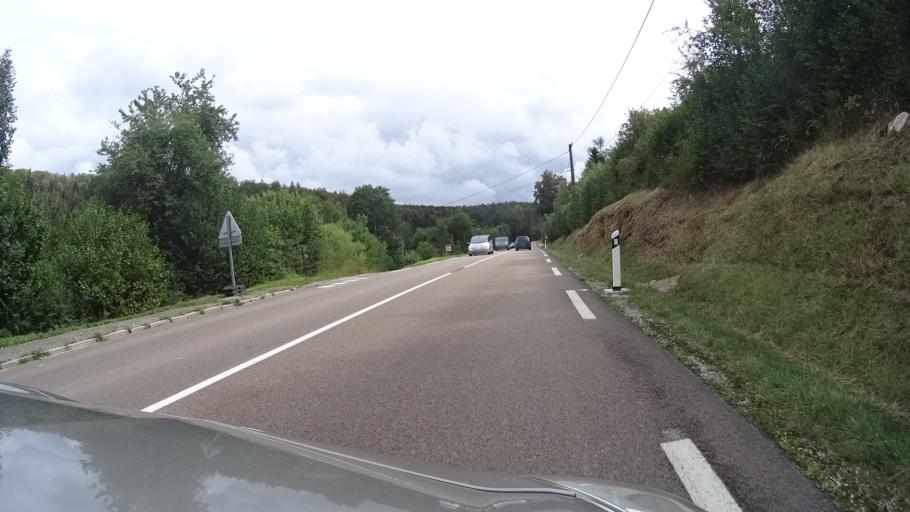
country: FR
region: Franche-Comte
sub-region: Departement du Jura
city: Champagnole
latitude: 46.6531
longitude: 5.9415
